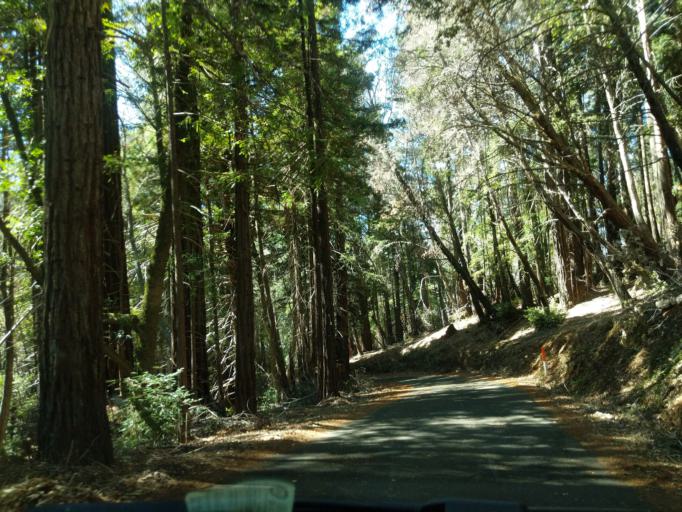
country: US
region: California
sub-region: Sonoma County
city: Monte Rio
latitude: 38.5254
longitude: -123.2294
